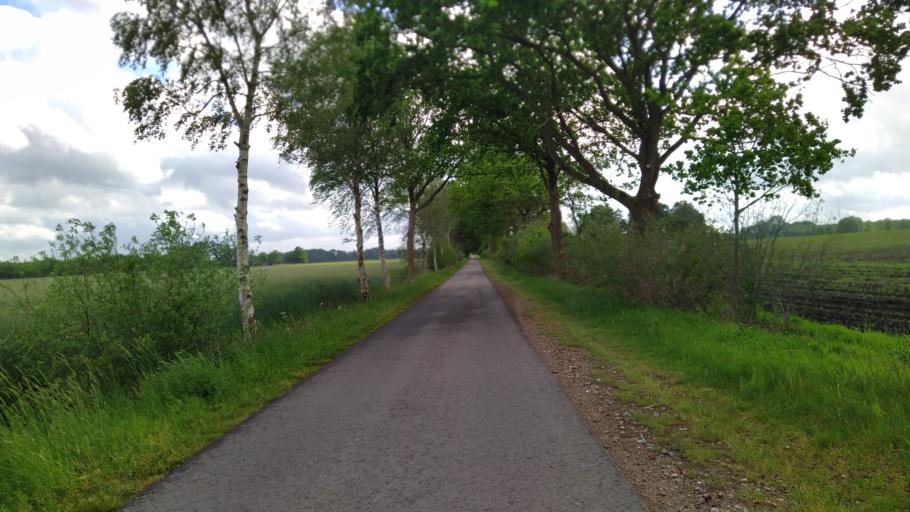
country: DE
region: Lower Saxony
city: Brest
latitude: 53.4435
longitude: 9.3661
